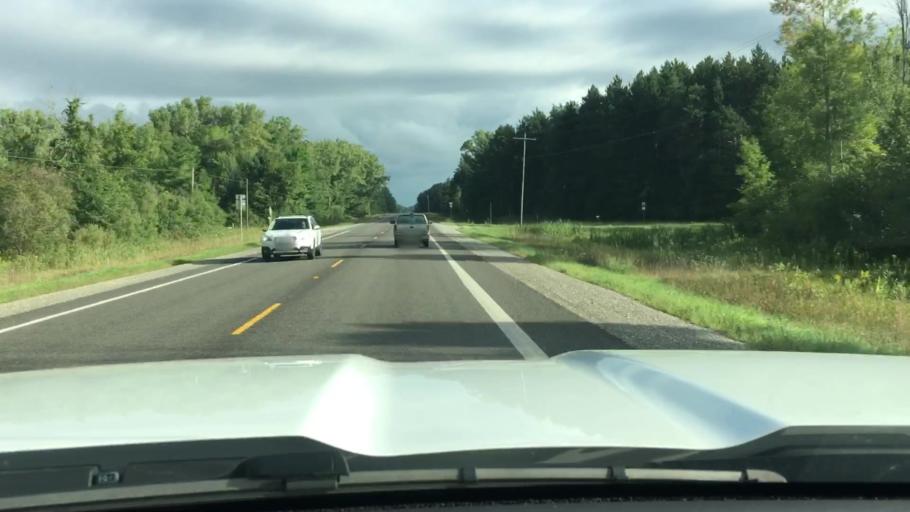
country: US
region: Michigan
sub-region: Tuscola County
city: Caro
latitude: 43.4228
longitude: -83.3845
